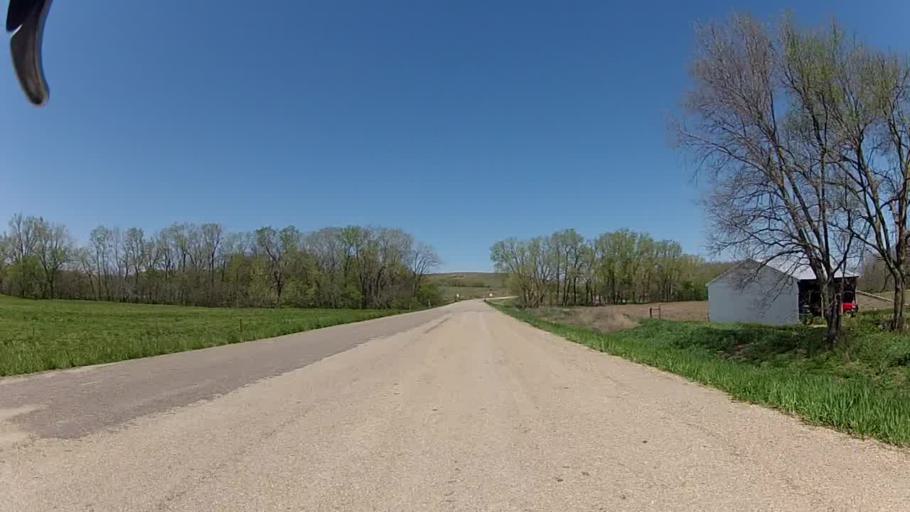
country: US
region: Kansas
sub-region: Riley County
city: Ogden
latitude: 38.9876
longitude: -96.5937
